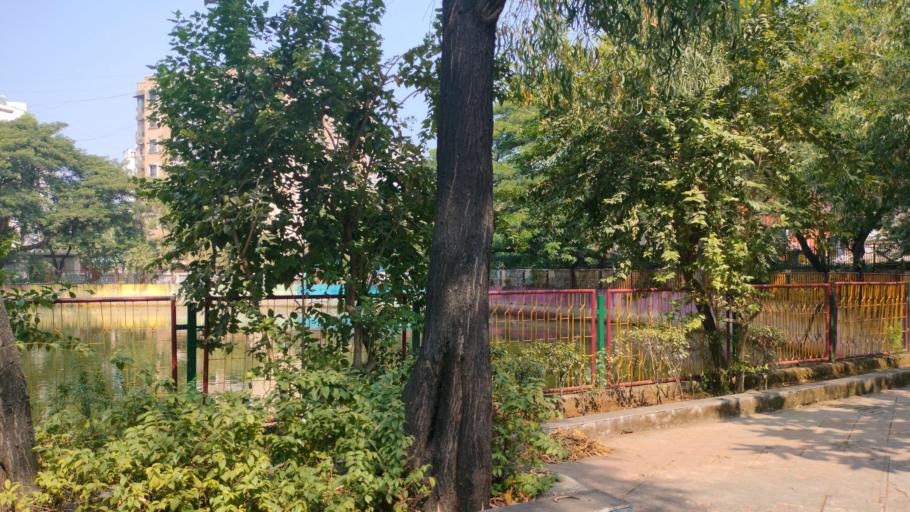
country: IN
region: Maharashtra
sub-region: Mumbai Suburban
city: Borivli
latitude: 19.2697
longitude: 72.8747
